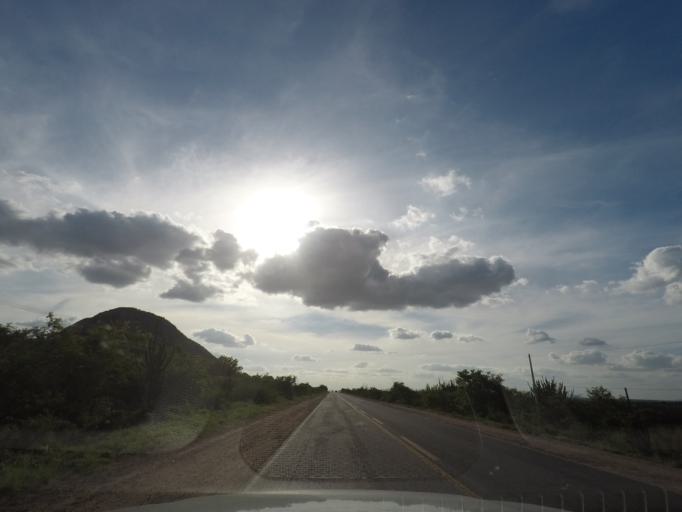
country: BR
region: Bahia
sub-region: Anguera
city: Anguera
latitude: -12.1821
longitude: -39.4604
